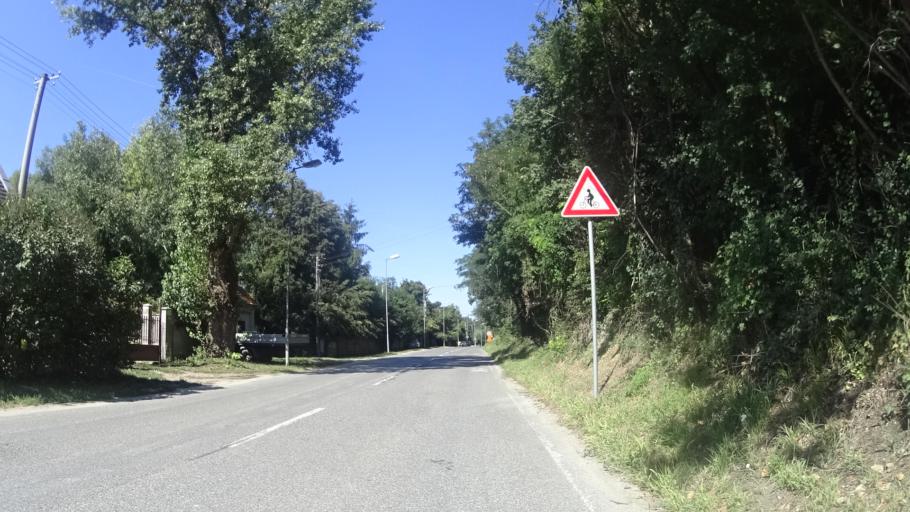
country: AT
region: Lower Austria
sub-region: Politischer Bezirk Bruck an der Leitha
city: Wolfsthal
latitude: 48.1518
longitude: 17.0309
